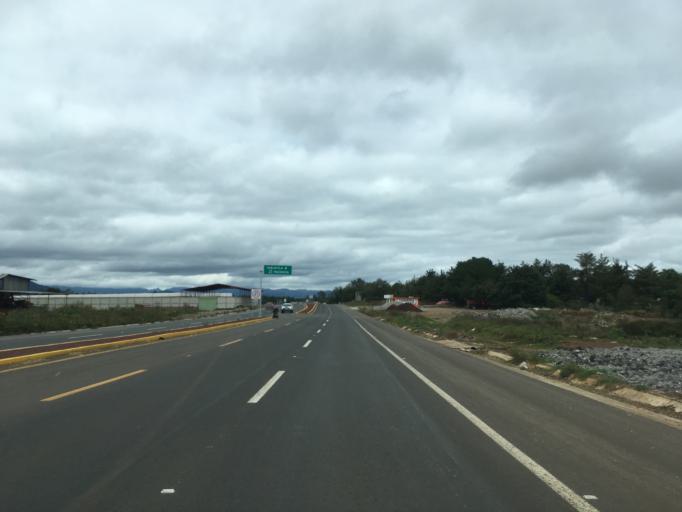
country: MX
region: Hidalgo
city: Atotonilco el Grande
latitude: 20.2961
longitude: -98.6695
